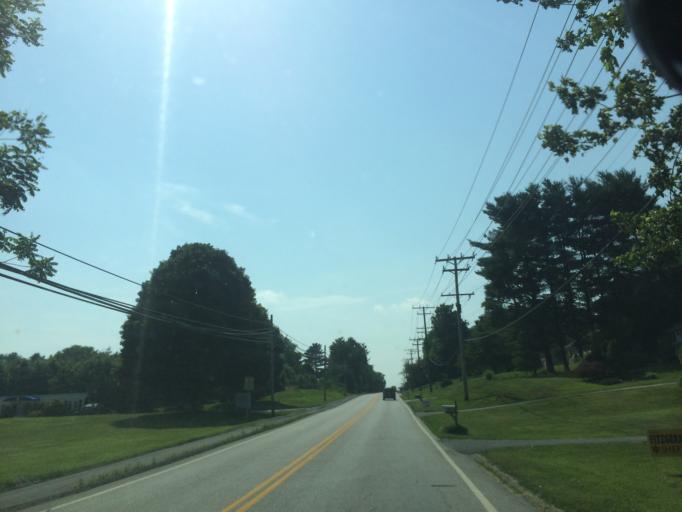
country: US
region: Maryland
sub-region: Howard County
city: Columbia
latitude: 39.2739
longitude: -76.8415
